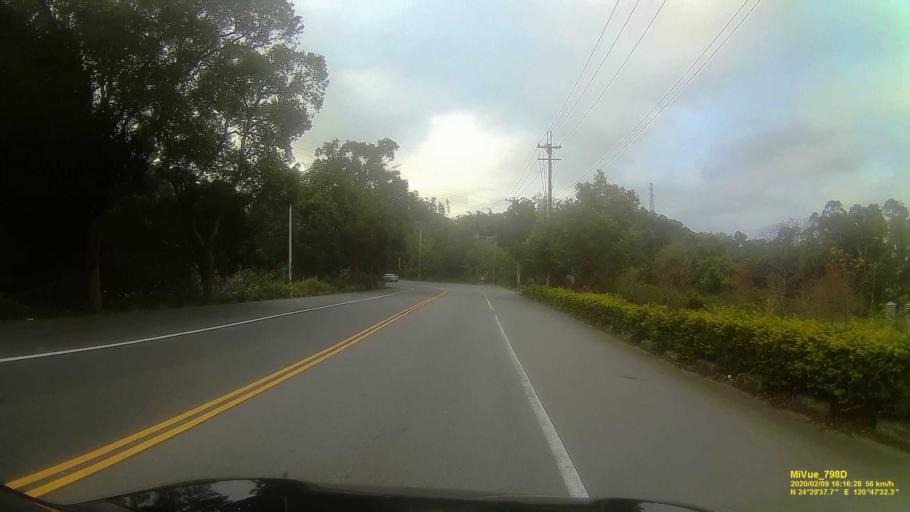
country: TW
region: Taiwan
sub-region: Miaoli
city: Miaoli
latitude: 24.4941
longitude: 120.7920
